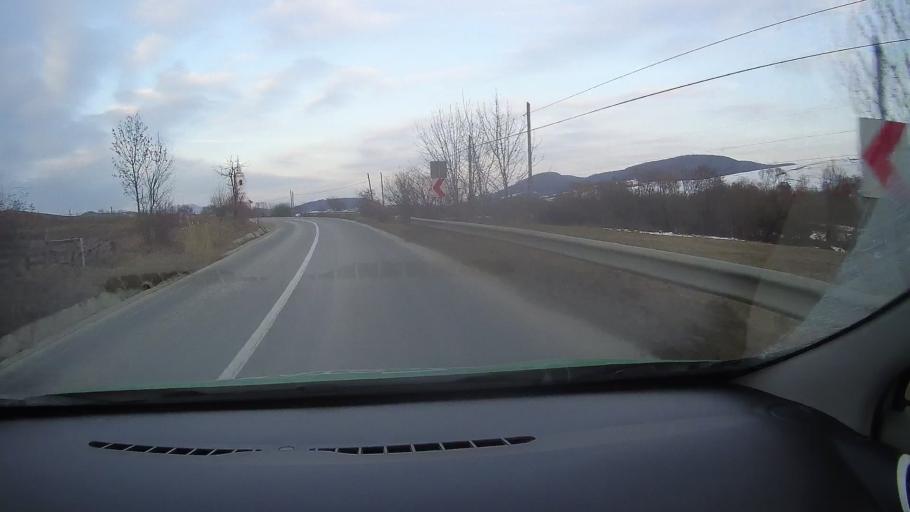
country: RO
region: Harghita
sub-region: Comuna Lupeni
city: Lupeni
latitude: 46.3570
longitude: 25.1656
